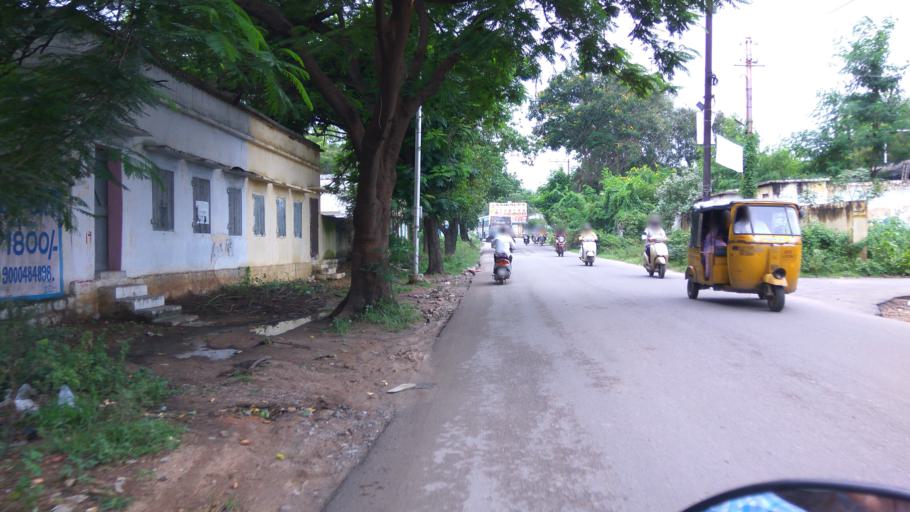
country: IN
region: Telangana
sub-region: Hyderabad
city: Malkajgiri
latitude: 17.4409
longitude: 78.5305
